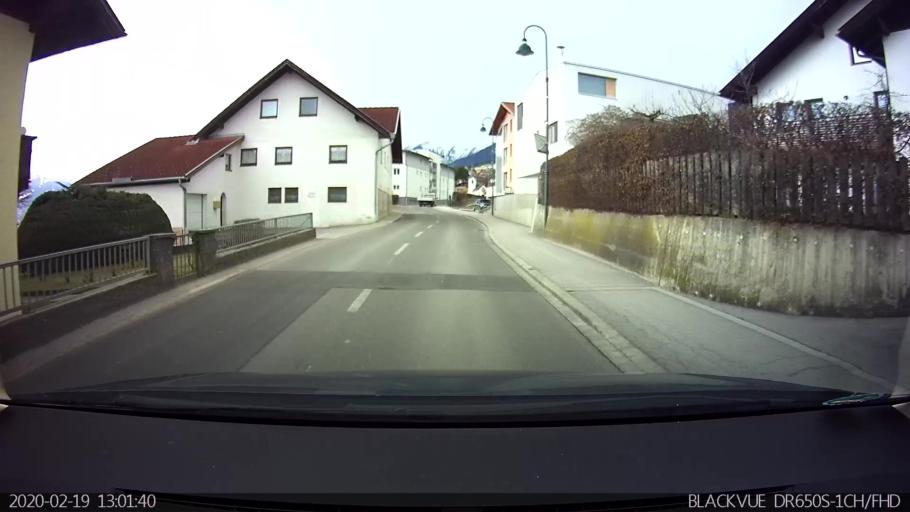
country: AT
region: Tyrol
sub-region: Politischer Bezirk Innsbruck Land
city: Rum
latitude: 47.2873
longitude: 11.4569
